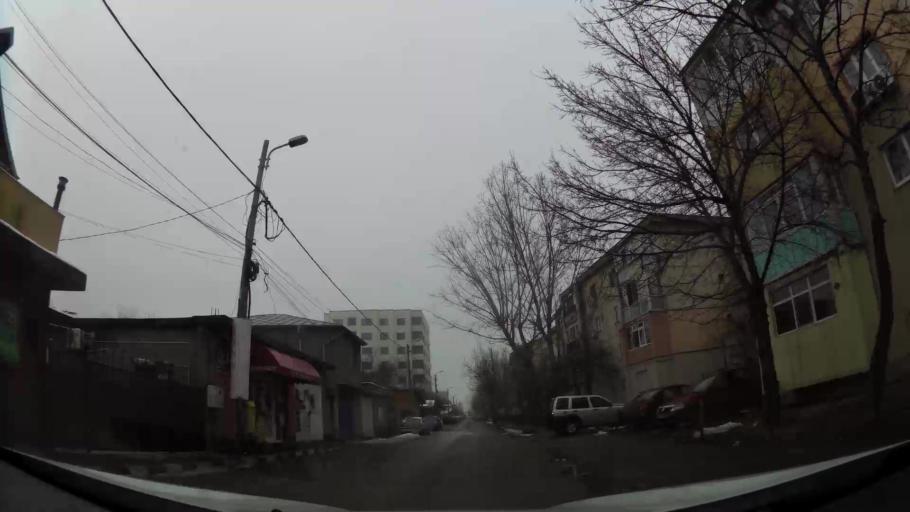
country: RO
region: Ilfov
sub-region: Comuna Chiajna
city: Rosu
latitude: 44.4379
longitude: 26.0050
